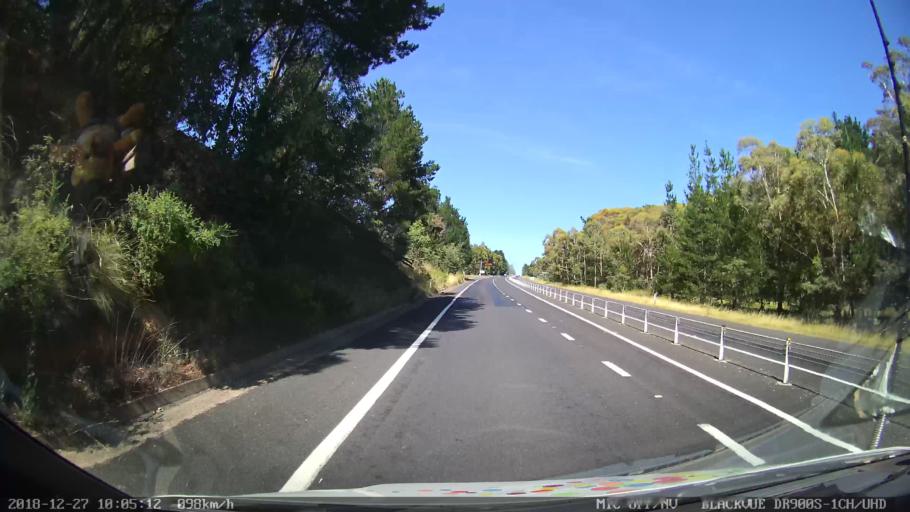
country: AU
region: New South Wales
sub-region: Lithgow
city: Portland
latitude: -33.4337
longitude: 149.8752
